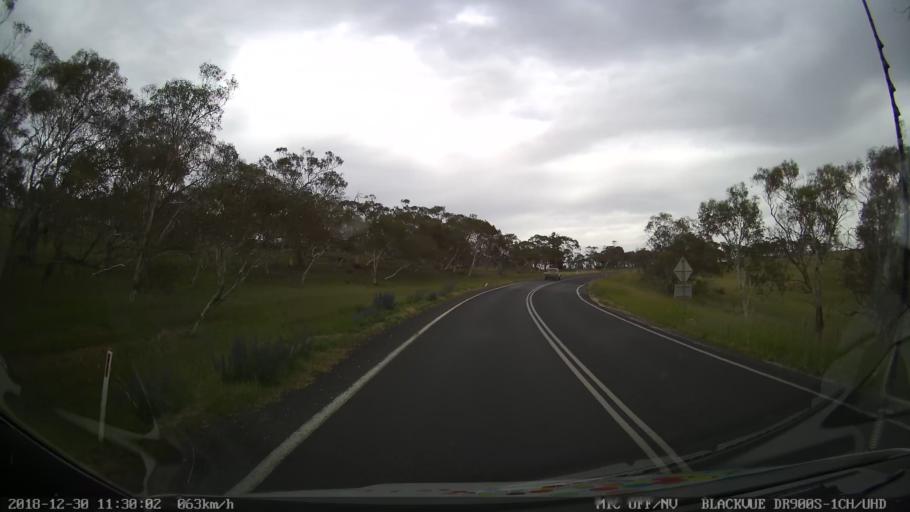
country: AU
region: New South Wales
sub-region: Snowy River
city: Jindabyne
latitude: -36.4460
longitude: 148.6071
